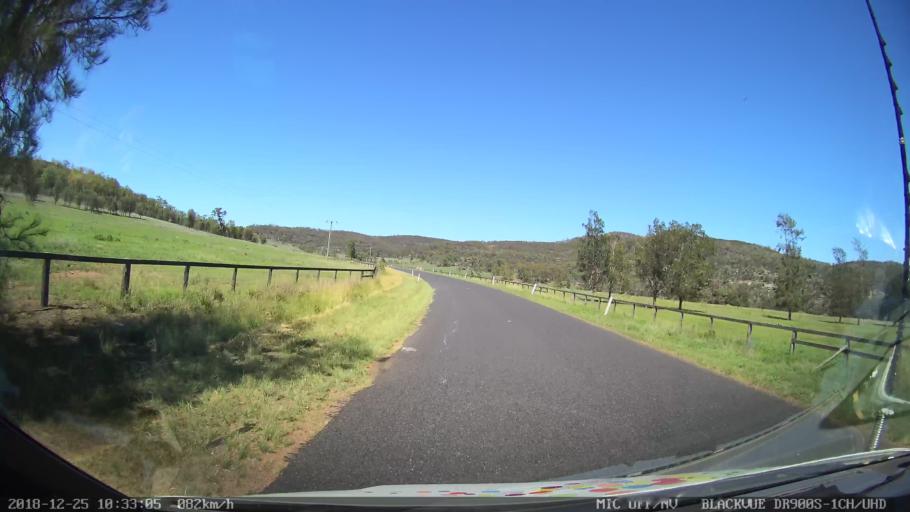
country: AU
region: New South Wales
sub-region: Upper Hunter Shire
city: Merriwa
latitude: -32.3794
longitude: 150.4099
